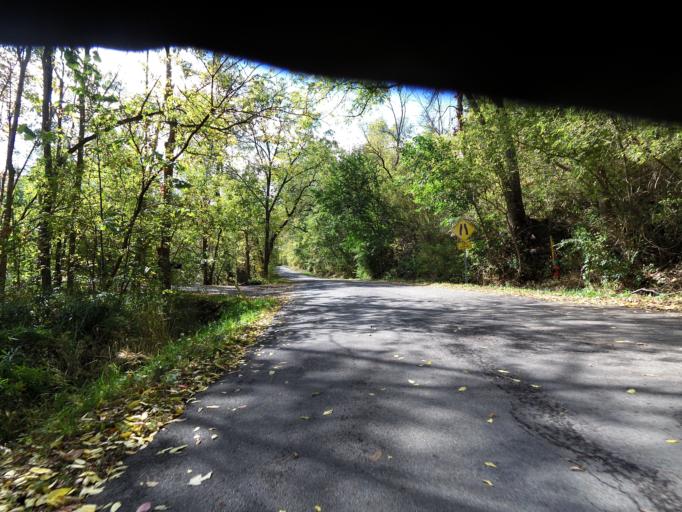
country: CA
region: Ontario
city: Hamilton
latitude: 43.3055
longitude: -79.9139
